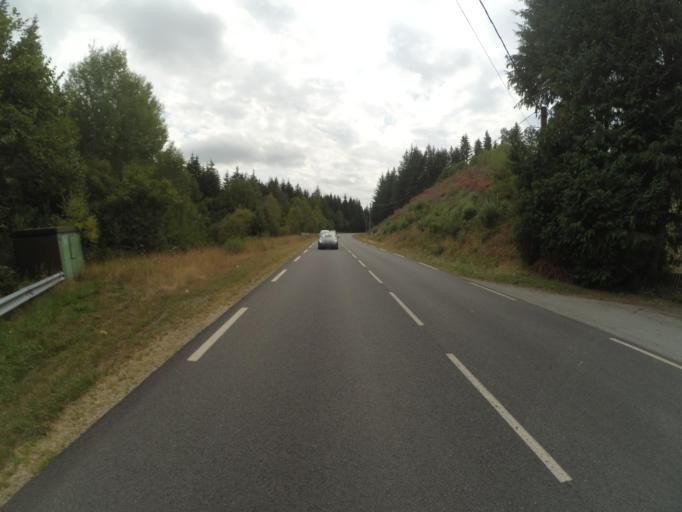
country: FR
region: Limousin
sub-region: Departement de la Creuse
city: La Courtine
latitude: 45.6429
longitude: 2.2733
